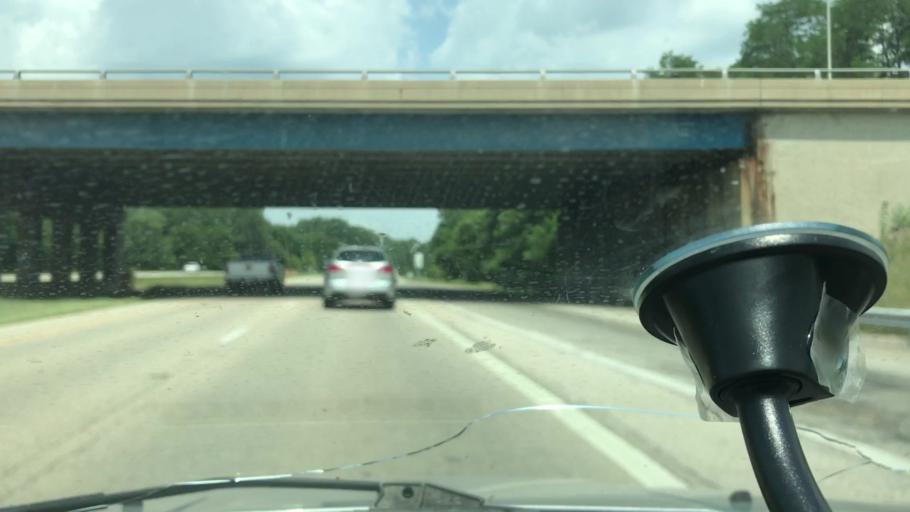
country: US
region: Illinois
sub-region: Peoria County
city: Bellevue
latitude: 40.6730
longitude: -89.6691
